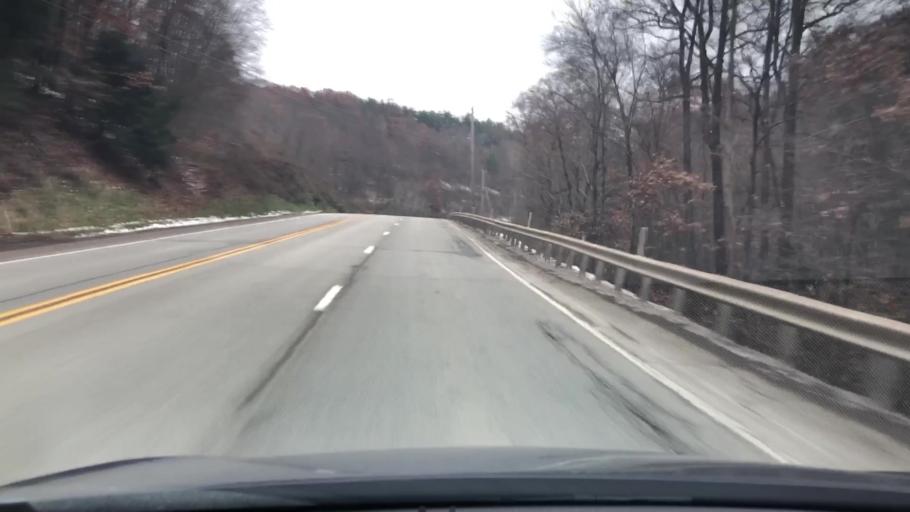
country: US
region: Pennsylvania
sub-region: Armstrong County
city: Kittanning
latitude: 40.8979
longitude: -79.3707
